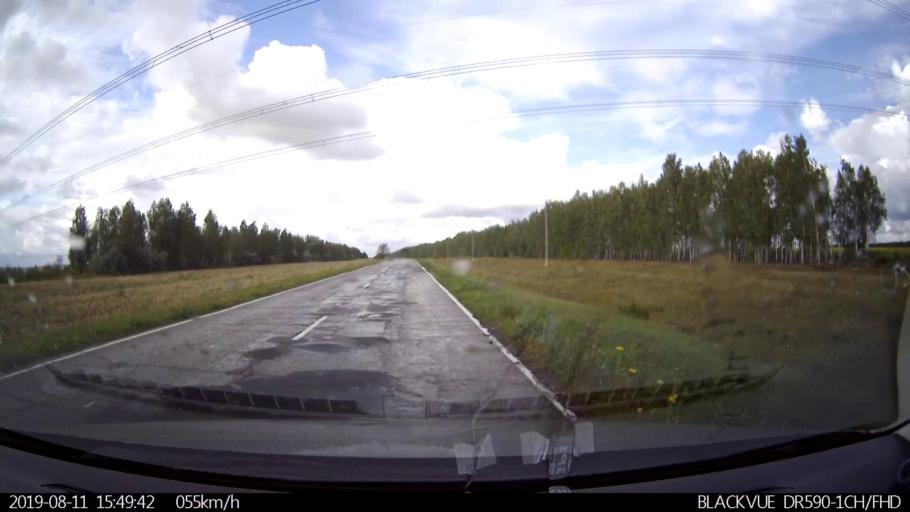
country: RU
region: Ulyanovsk
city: Ignatovka
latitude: 53.9064
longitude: 47.6553
